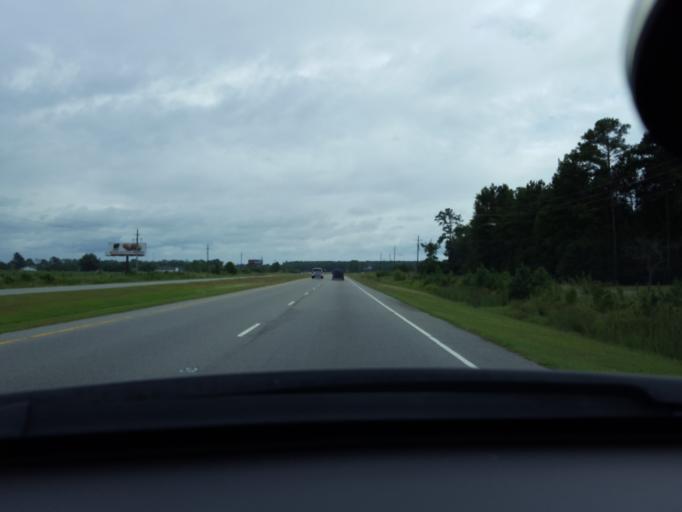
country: US
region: North Carolina
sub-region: Pitt County
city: Ayden
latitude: 35.4722
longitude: -77.4358
